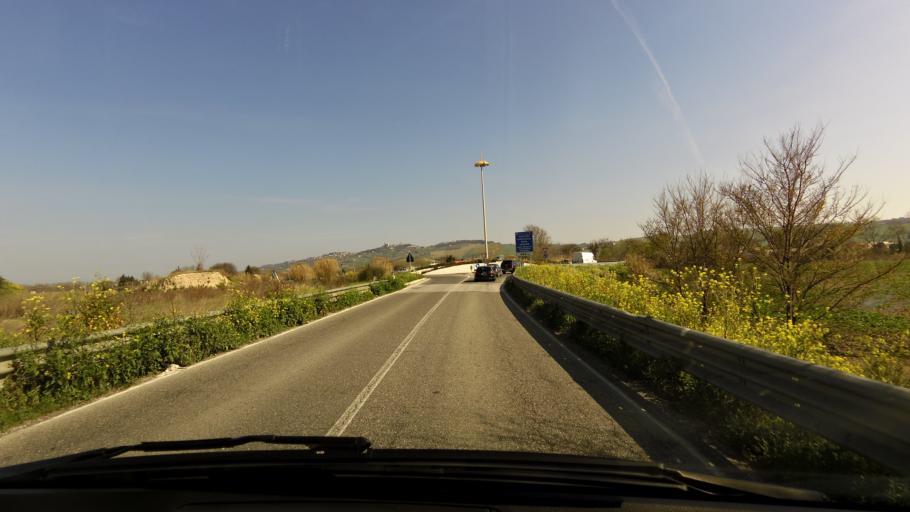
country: IT
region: The Marches
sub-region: Provincia di Macerata
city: Montelupone
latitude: 43.3752
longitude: 13.5754
